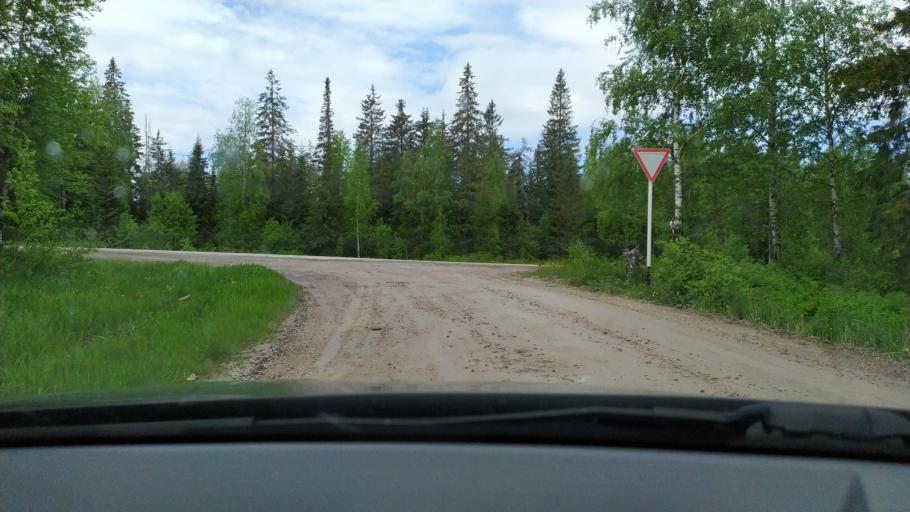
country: RU
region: Perm
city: Gremyachinsk
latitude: 58.5110
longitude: 57.8125
